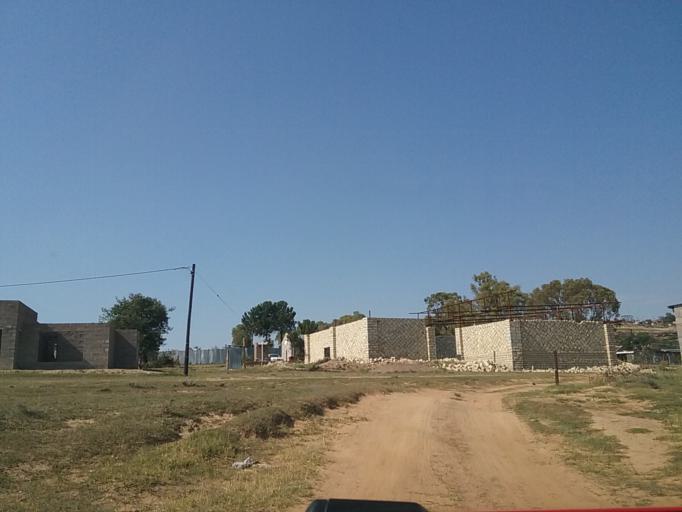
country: LS
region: Berea
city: Teyateyaneng
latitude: -29.1312
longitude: 27.7585
